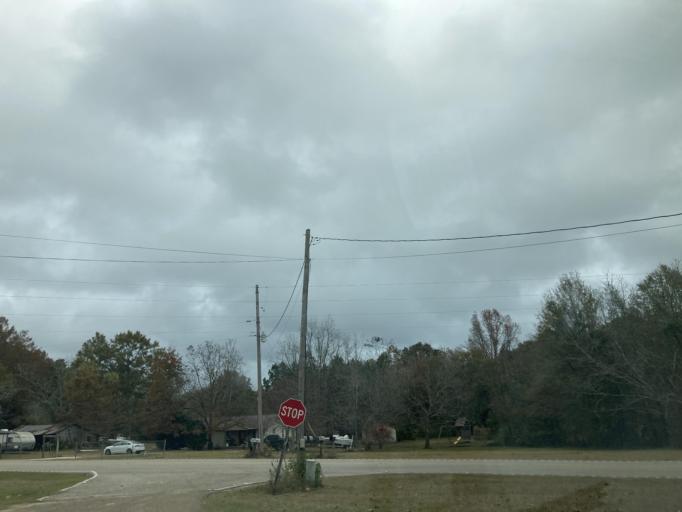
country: US
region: Mississippi
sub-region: Lamar County
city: Lumberton
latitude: 31.0860
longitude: -89.5941
